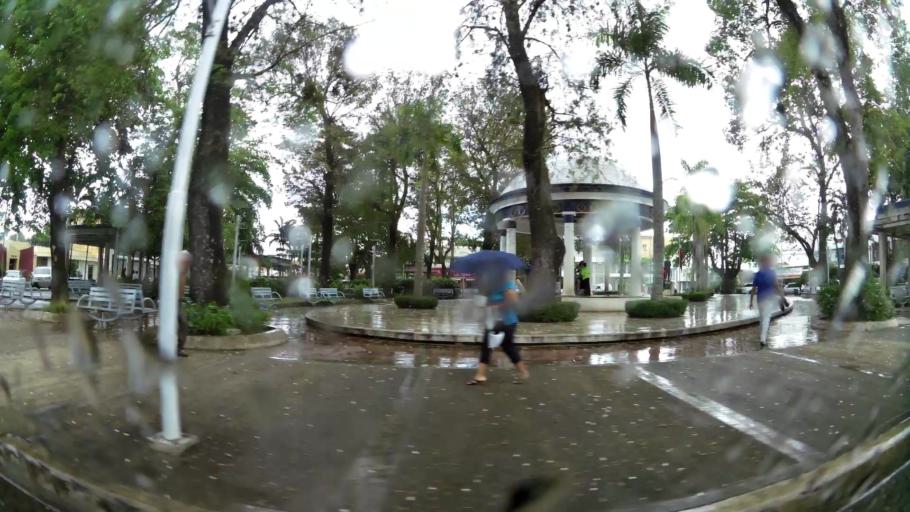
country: DO
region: Monsenor Nouel
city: Bonao
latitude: 18.9421
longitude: -70.4116
